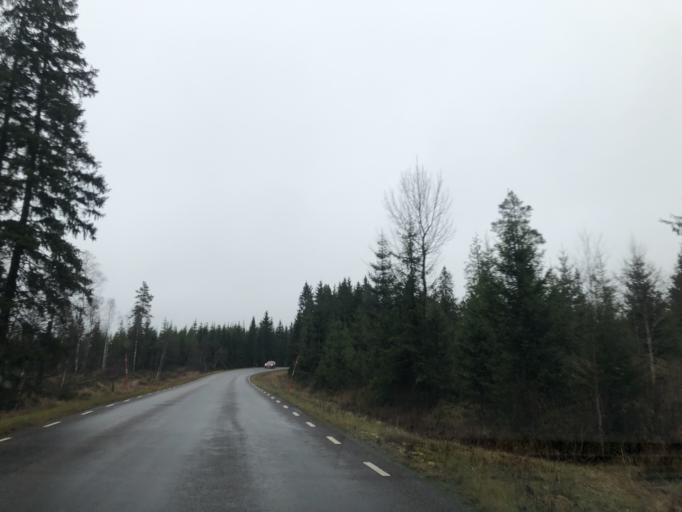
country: SE
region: Vaestra Goetaland
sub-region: Ulricehamns Kommun
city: Ulricehamn
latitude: 57.7454
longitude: 13.5332
